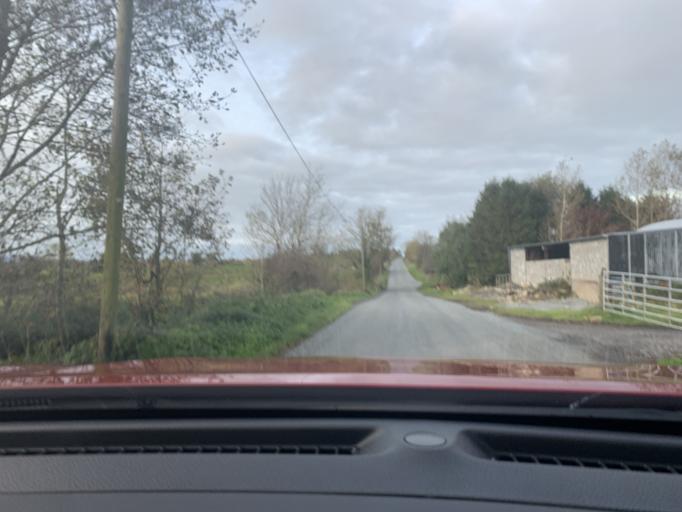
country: IE
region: Connaught
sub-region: Roscommon
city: Ballaghaderreen
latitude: 53.9849
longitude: -8.6149
